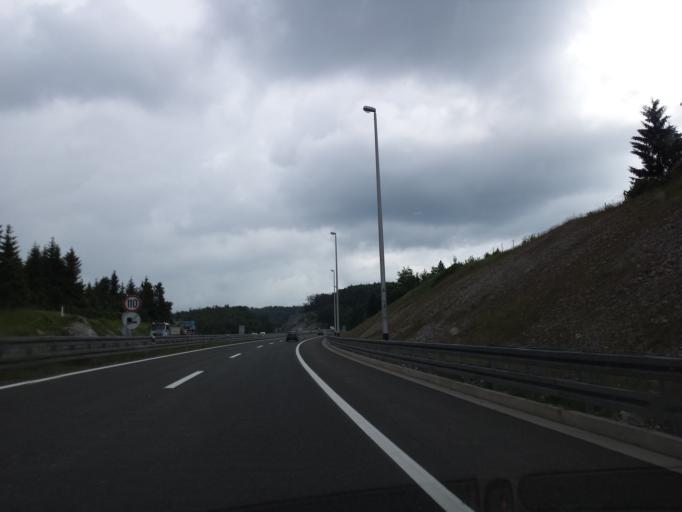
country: HR
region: Primorsko-Goranska
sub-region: Grad Delnice
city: Delnice
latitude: 45.3873
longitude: 14.8064
